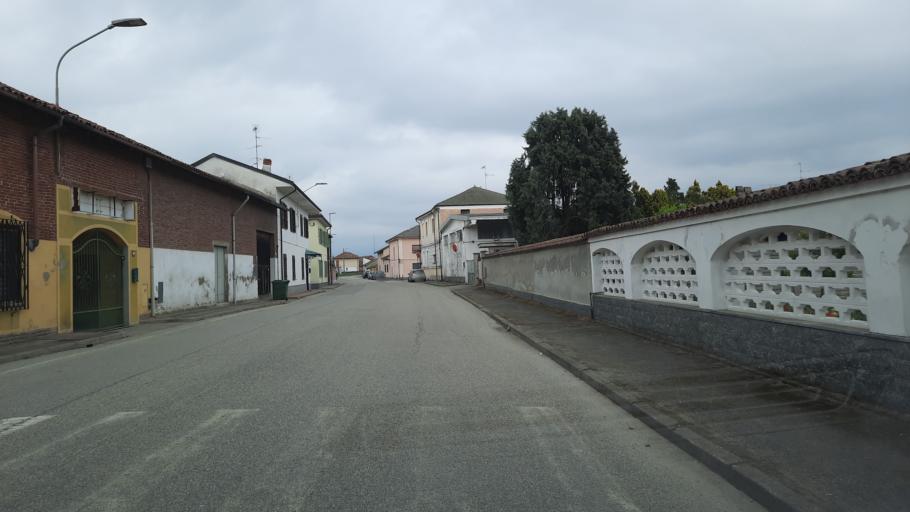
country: IT
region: Lombardy
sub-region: Provincia di Pavia
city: Castelnovetto
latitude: 45.2545
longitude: 8.6104
